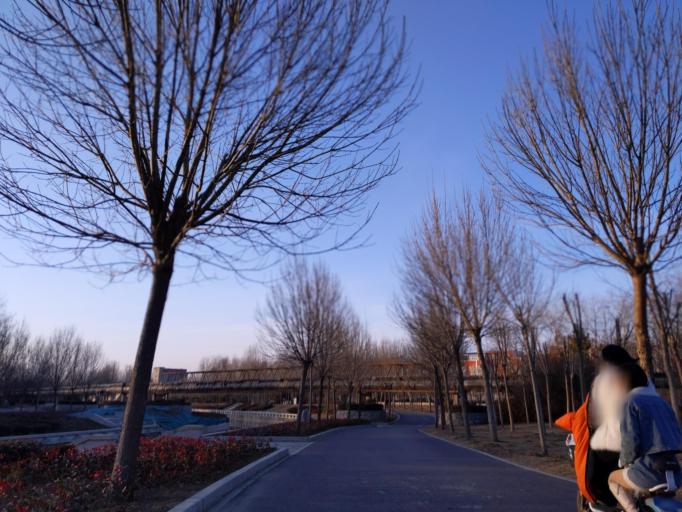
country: CN
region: Henan Sheng
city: Puyang
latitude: 35.7692
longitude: 114.9984
